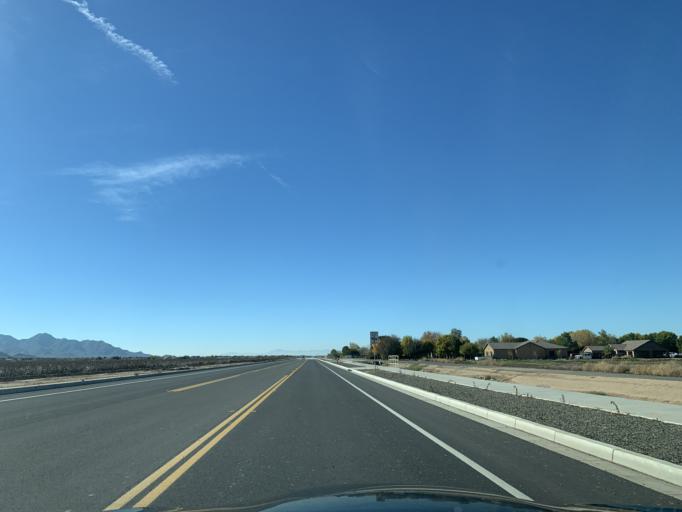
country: US
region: Arizona
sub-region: Maricopa County
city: Queen Creek
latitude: 33.2197
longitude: -111.6004
